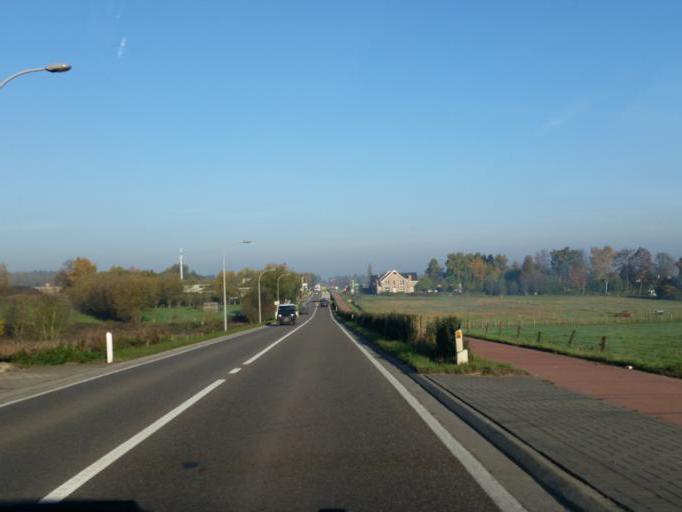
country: BE
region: Flanders
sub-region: Provincie Vlaams-Brabant
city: Asse
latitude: 50.9254
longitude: 4.1822
